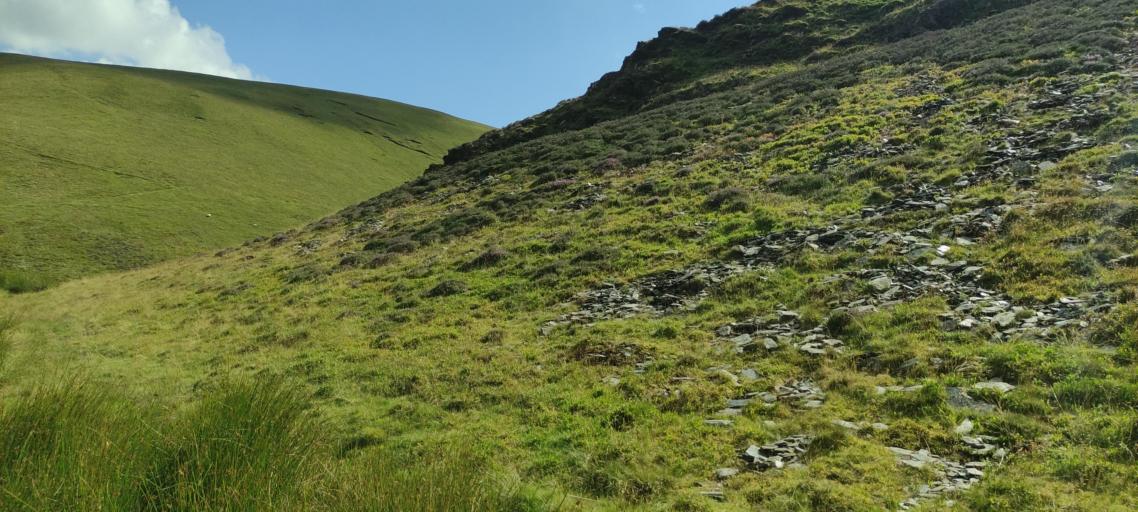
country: GB
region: England
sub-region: Cumbria
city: Keswick
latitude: 54.6913
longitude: -3.1204
